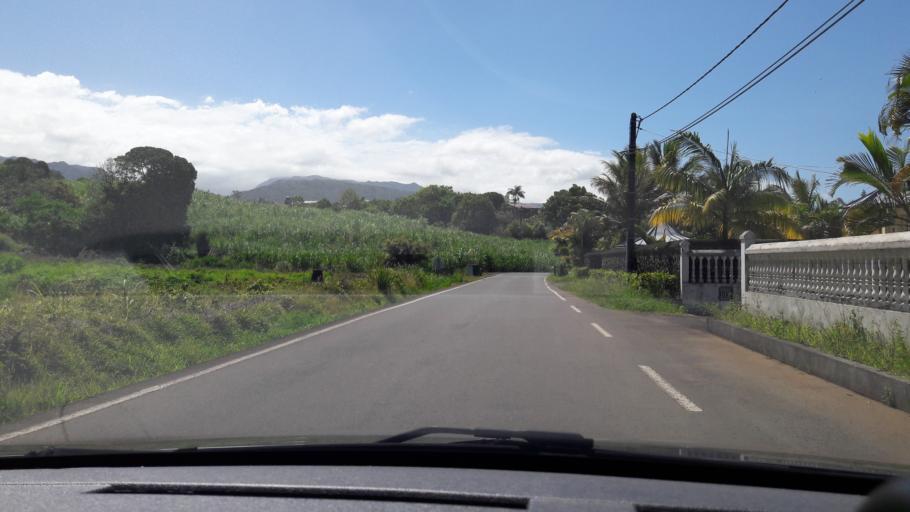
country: RE
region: Reunion
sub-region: Reunion
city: Saint-Benoit
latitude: -21.0948
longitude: 55.7067
